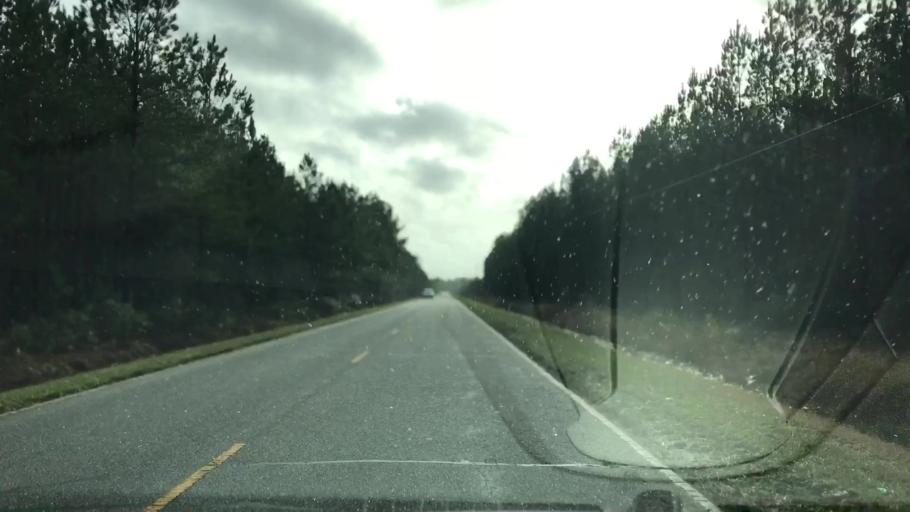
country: US
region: South Carolina
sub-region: Williamsburg County
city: Andrews
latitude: 33.4167
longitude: -79.6038
